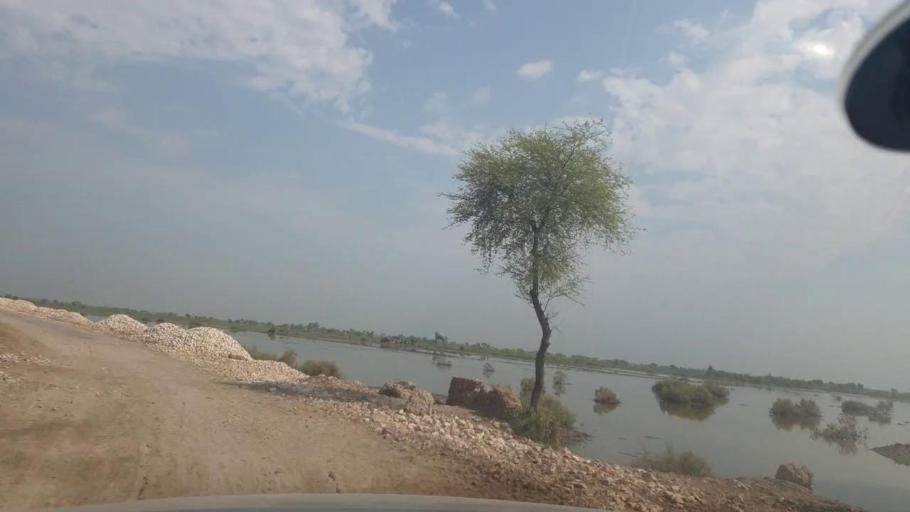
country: PK
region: Balochistan
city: Mehrabpur
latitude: 28.0789
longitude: 68.1011
